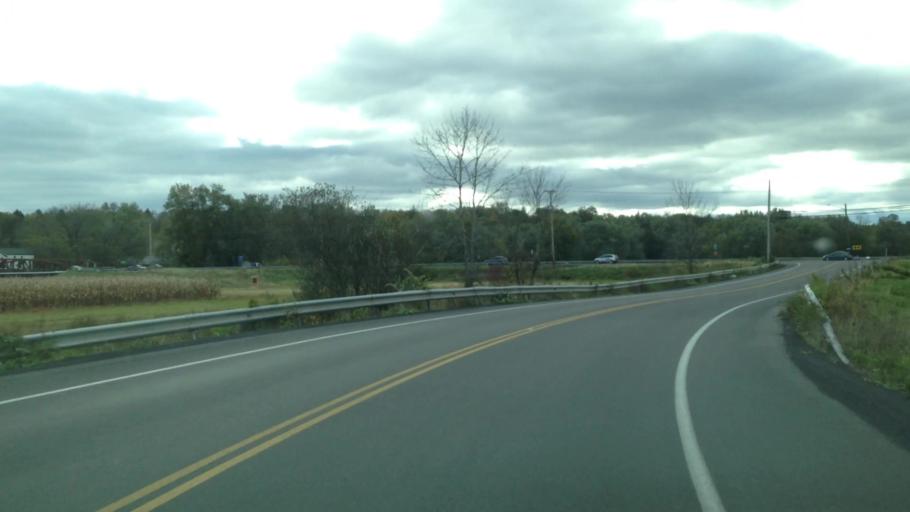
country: US
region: New York
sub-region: Ulster County
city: New Paltz
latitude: 41.7484
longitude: -74.0927
